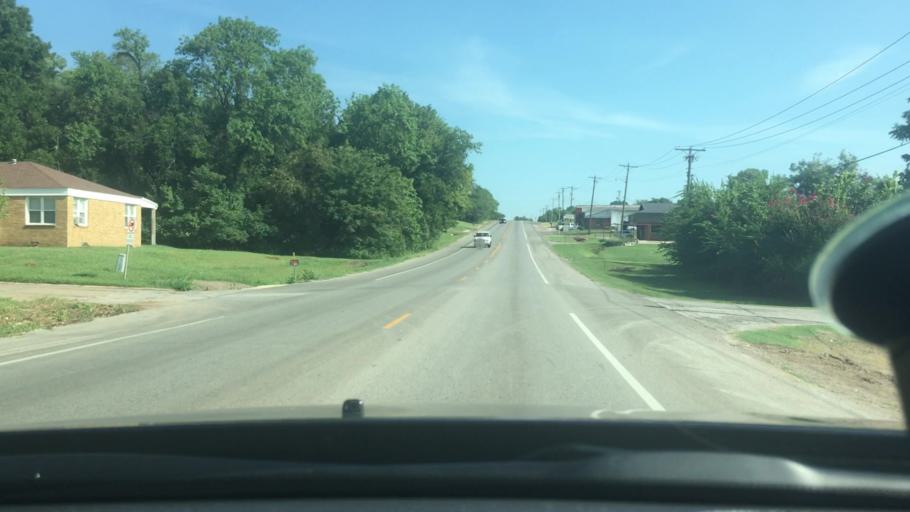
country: US
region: Oklahoma
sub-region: Garvin County
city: Pauls Valley
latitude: 34.7219
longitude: -97.2129
